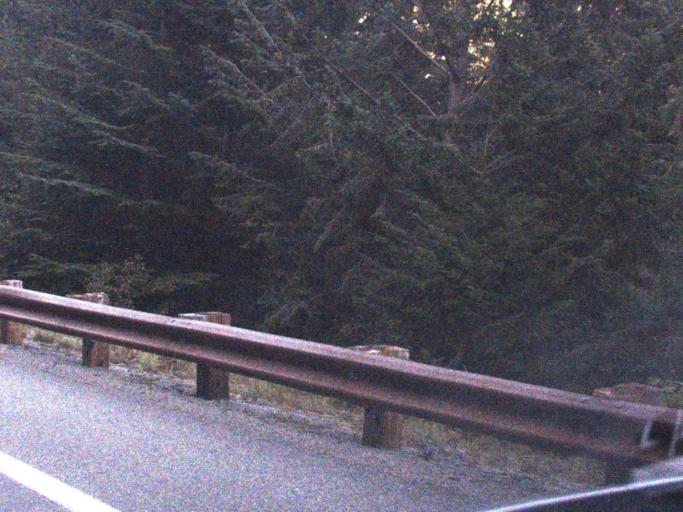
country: US
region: Washington
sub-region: Snohomish County
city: Darrington
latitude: 48.6320
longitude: -120.8460
